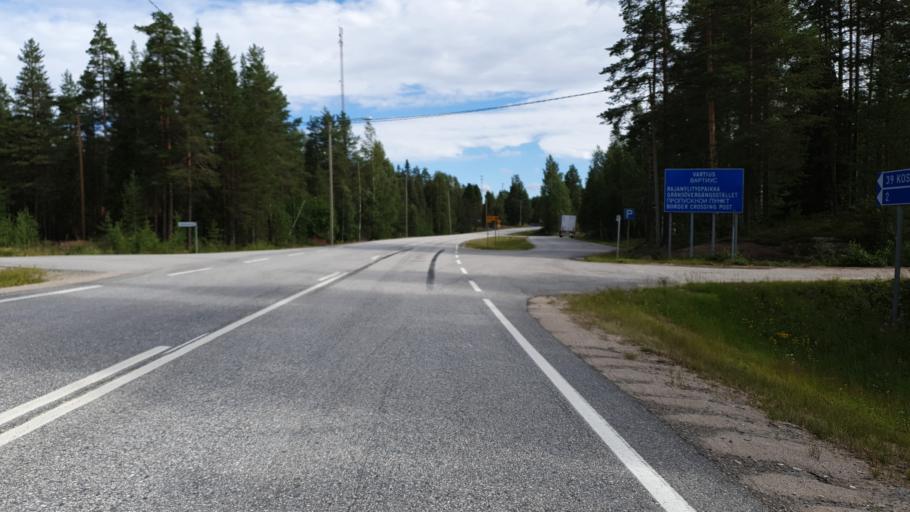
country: FI
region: Kainuu
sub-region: Kehys-Kainuu
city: Kuhmo
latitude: 64.5372
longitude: 29.9454
